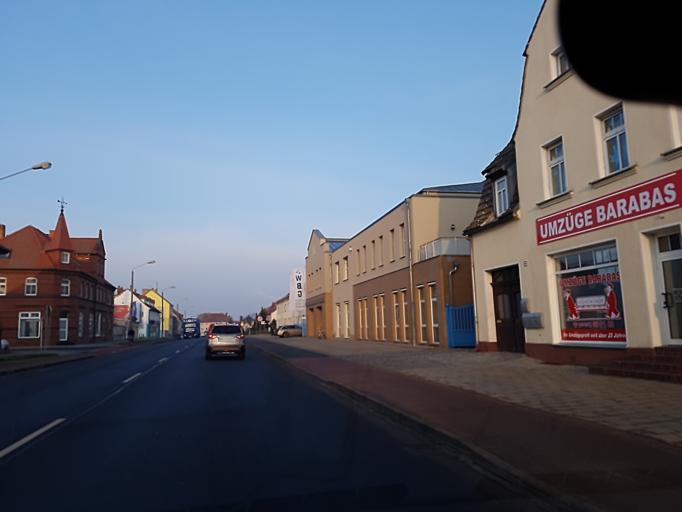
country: DE
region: Saxony-Anhalt
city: Wittenburg
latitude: 51.8667
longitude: 12.6068
